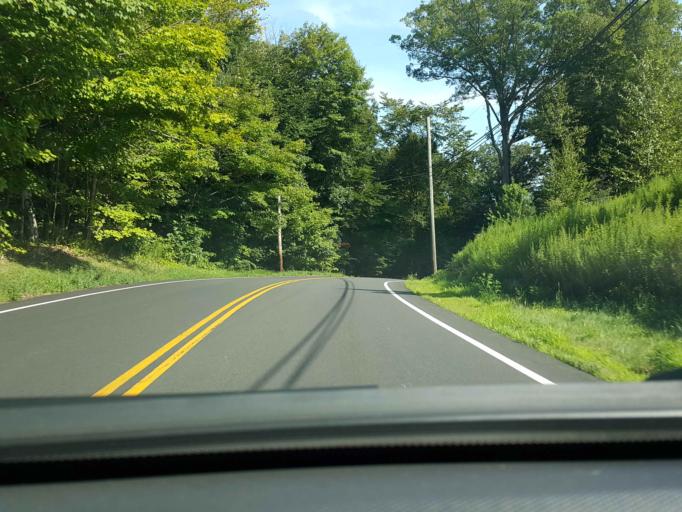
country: US
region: Connecticut
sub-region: Middlesex County
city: Durham
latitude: 41.4268
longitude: -72.6923
